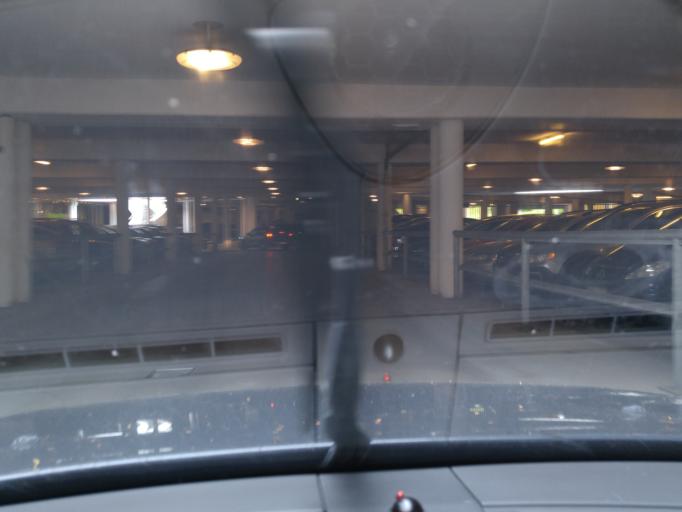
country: SE
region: Vaestra Goetaland
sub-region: Goteborg
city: Majorna
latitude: 57.6530
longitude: 11.9145
